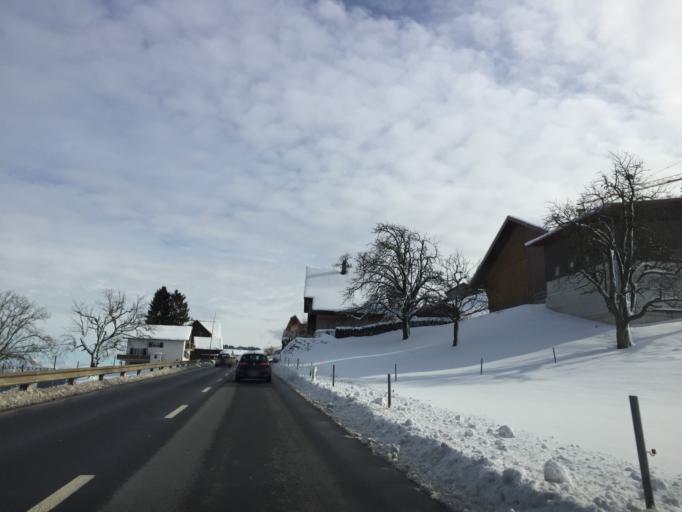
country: CH
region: Schwyz
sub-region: Bezirk Hoefe
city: Schindellegi
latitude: 47.1824
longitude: 8.6911
